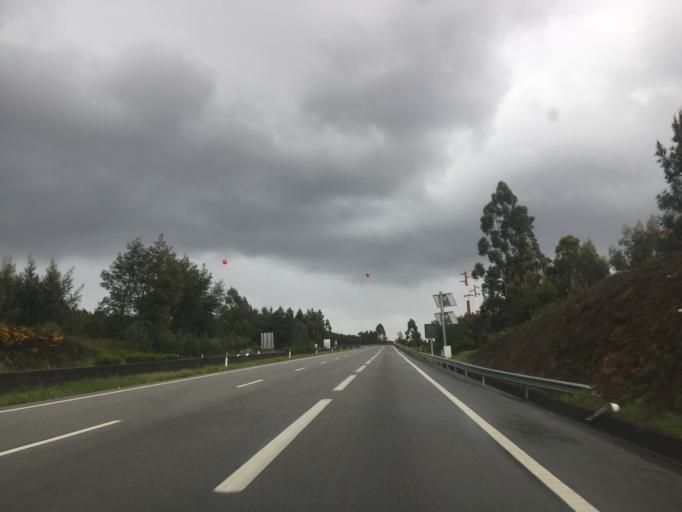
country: PT
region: Aveiro
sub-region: Agueda
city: Valongo
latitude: 40.6641
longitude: -8.3957
